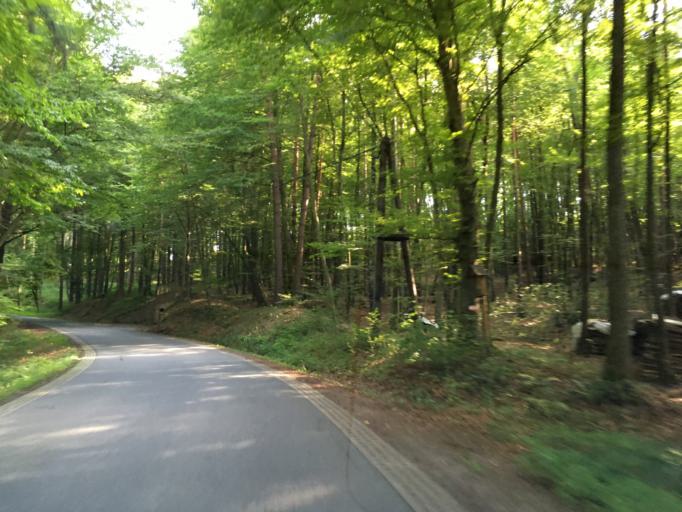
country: AT
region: Styria
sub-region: Politischer Bezirk Leibnitz
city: Sankt Nikolai im Sausal
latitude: 46.8068
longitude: 15.4574
